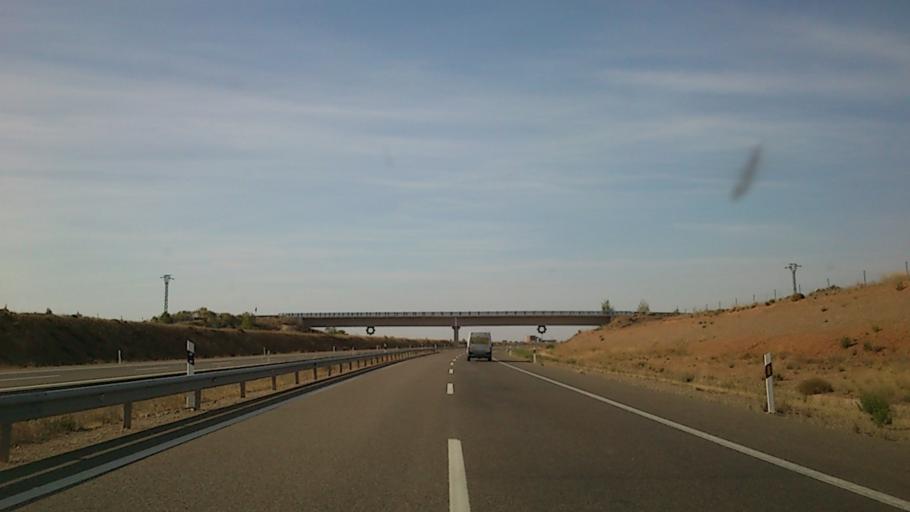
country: ES
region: Aragon
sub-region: Provincia de Zaragoza
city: Carinena
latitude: 41.3393
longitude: -1.2063
